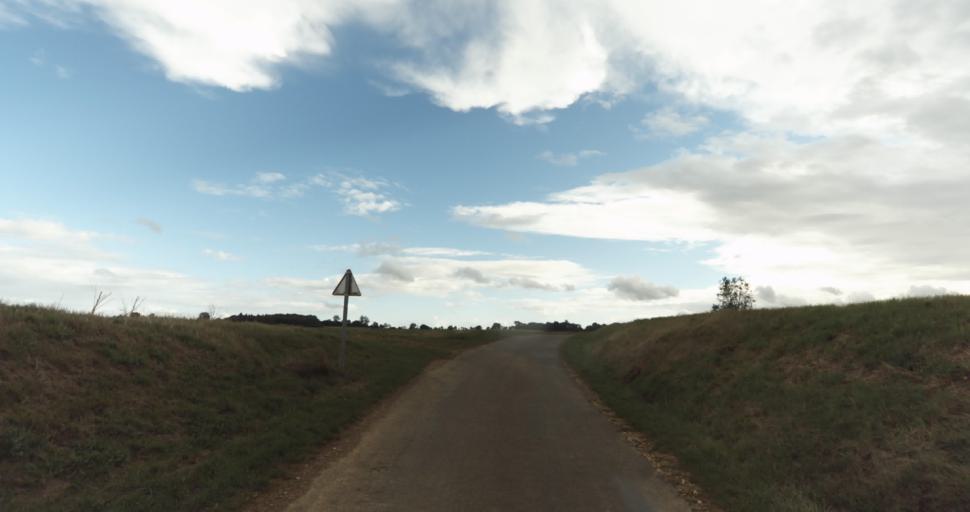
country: FR
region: Lower Normandy
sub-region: Departement de l'Orne
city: Sainte-Gauburge-Sainte-Colombe
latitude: 48.7361
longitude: 0.4059
